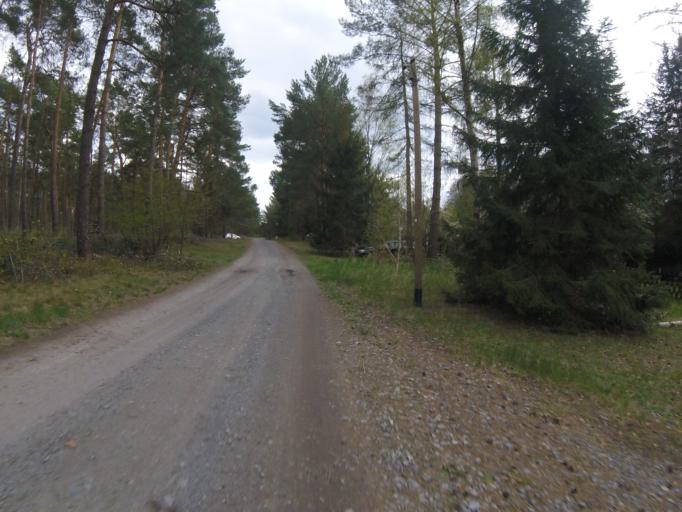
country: DE
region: Brandenburg
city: Schwerin
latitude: 52.1716
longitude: 13.6374
